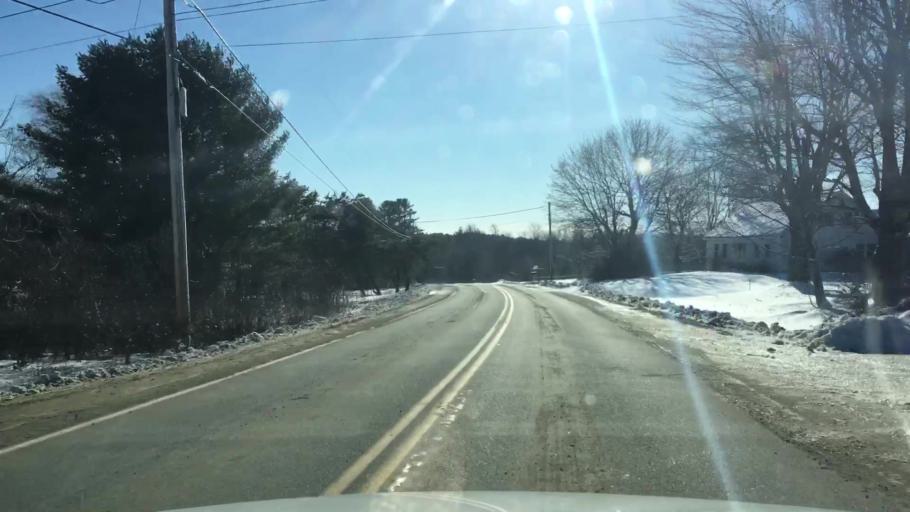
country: US
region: Maine
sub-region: Kennebec County
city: Readfield
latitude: 44.3618
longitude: -69.9901
